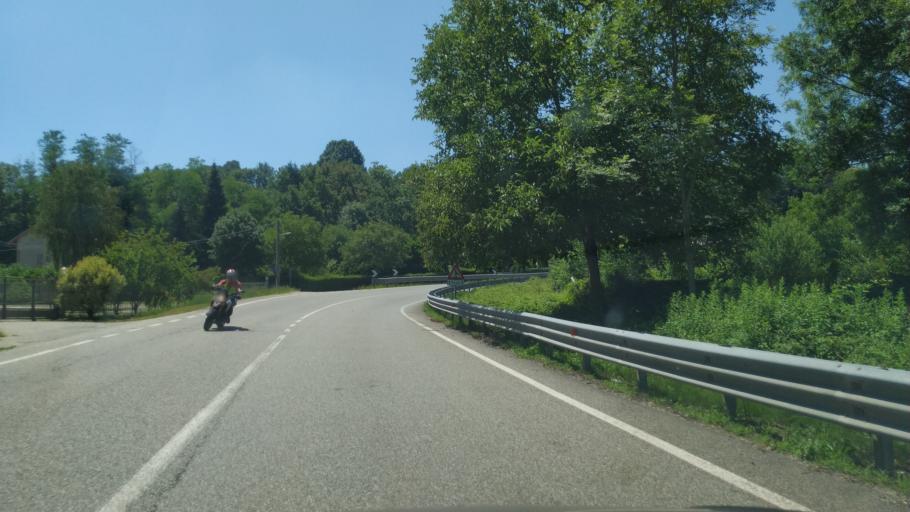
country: IT
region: Piedmont
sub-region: Provincia di Novara
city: Cureggio
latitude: 45.6687
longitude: 8.4527
